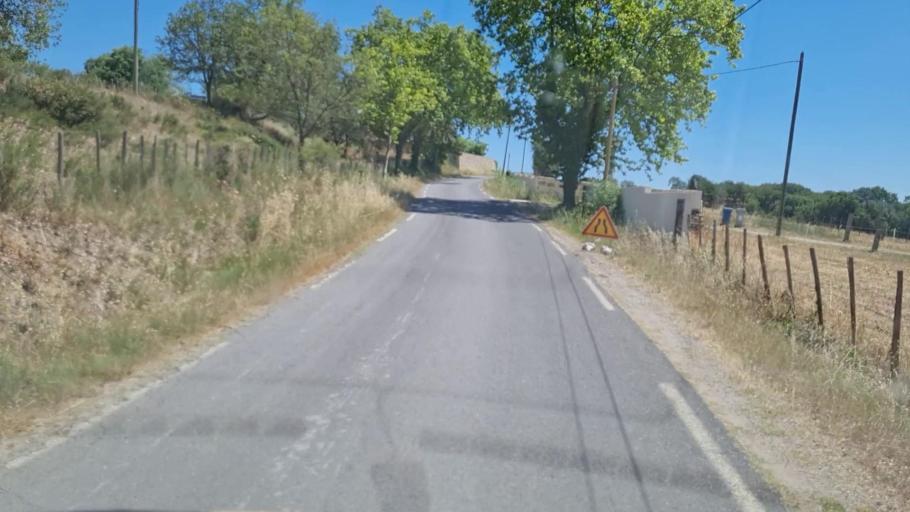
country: FR
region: Languedoc-Roussillon
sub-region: Departement du Gard
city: Le Cailar
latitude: 43.6421
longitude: 4.2528
